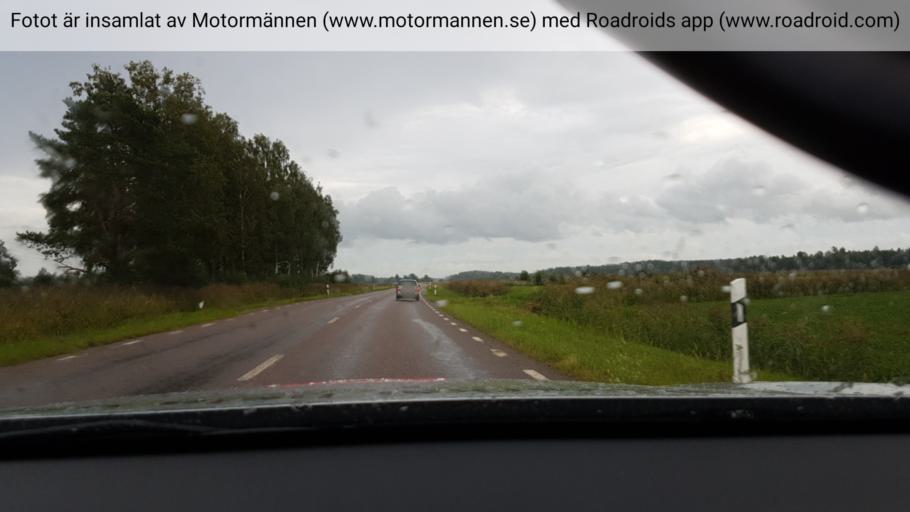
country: SE
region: Uppsala
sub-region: Tierps Kommun
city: Karlholmsbruk
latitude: 60.4989
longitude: 17.6870
